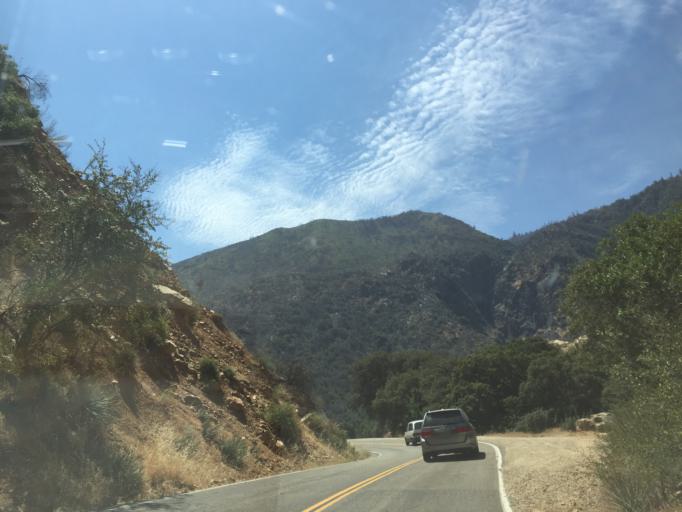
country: US
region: California
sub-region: Tulare County
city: Three Rivers
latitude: 36.8203
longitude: -118.8345
